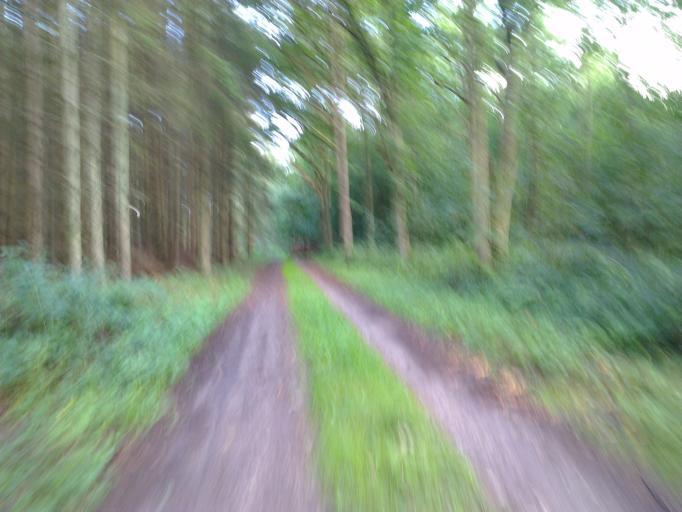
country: DK
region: Capital Region
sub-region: Frederikssund Kommune
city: Jaegerspris
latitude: 55.8945
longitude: 11.9942
